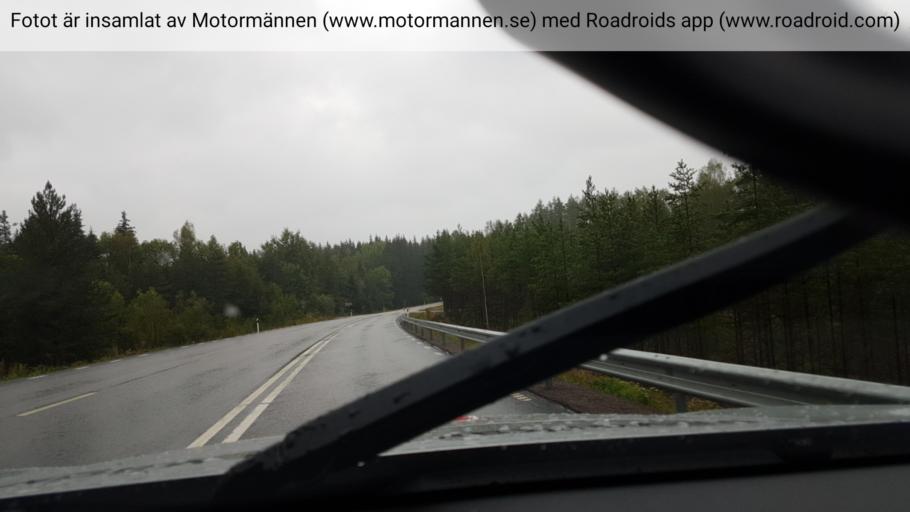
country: SE
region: Vaestra Goetaland
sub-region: Bengtsfors Kommun
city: Dals Langed
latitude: 58.8515
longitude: 12.1680
